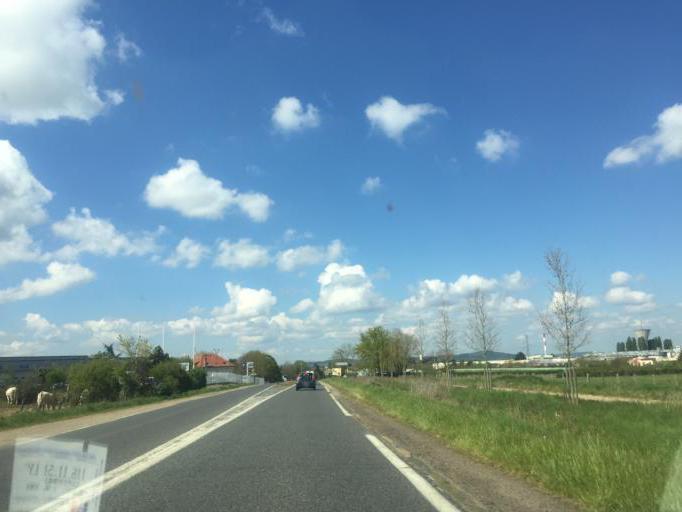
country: FR
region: Bourgogne
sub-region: Departement de l'Yonne
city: Avallon
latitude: 47.4930
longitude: 3.9305
